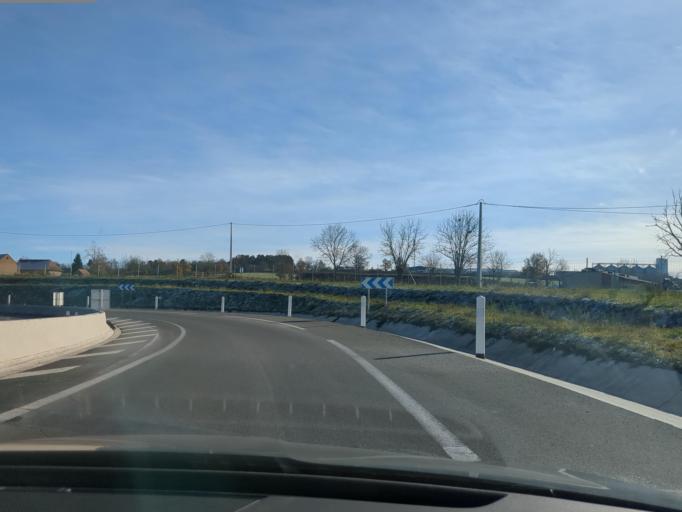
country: FR
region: Auvergne
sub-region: Departement de l'Allier
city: Montmarault
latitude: 46.3291
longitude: 2.9589
